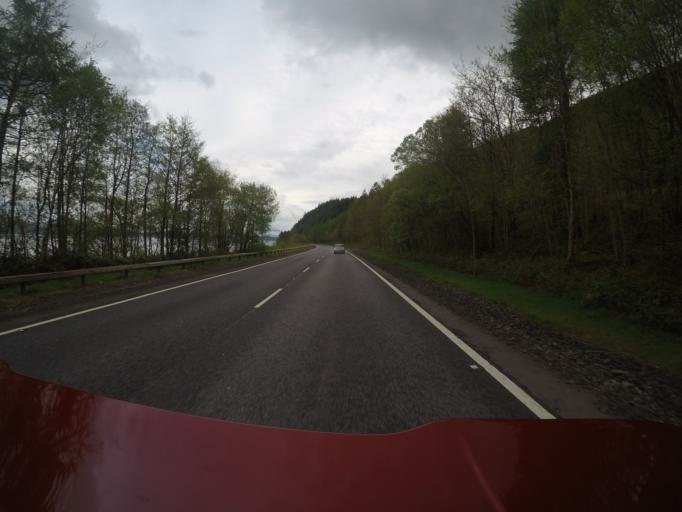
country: GB
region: Scotland
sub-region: Argyll and Bute
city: Helensburgh
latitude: 56.1203
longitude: -4.6508
